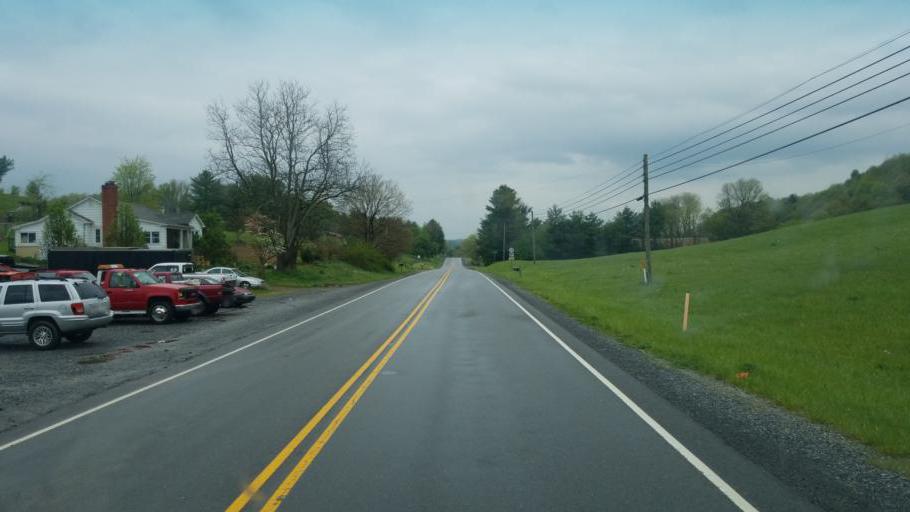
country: US
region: Virginia
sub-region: Wythe County
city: Rural Retreat
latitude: 36.8906
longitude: -81.3495
